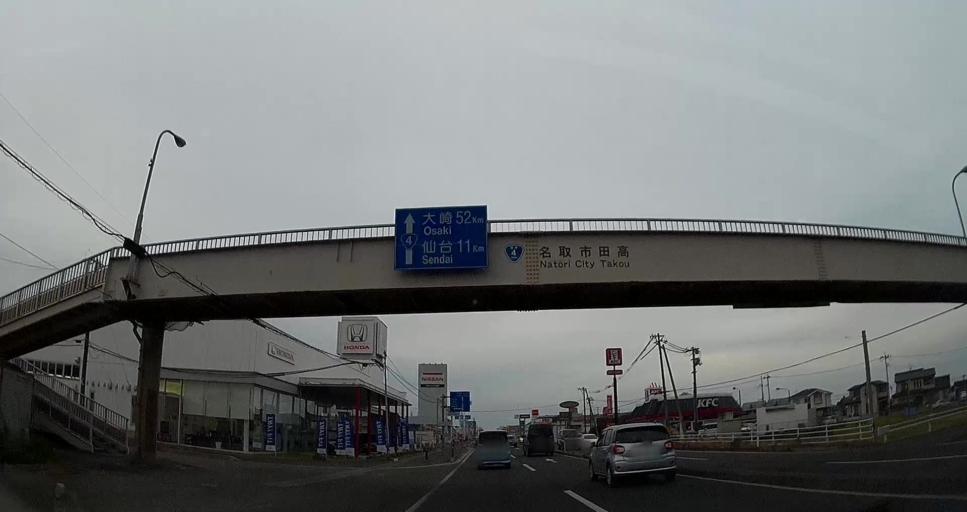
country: JP
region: Miyagi
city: Iwanuma
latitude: 38.1776
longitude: 140.8905
